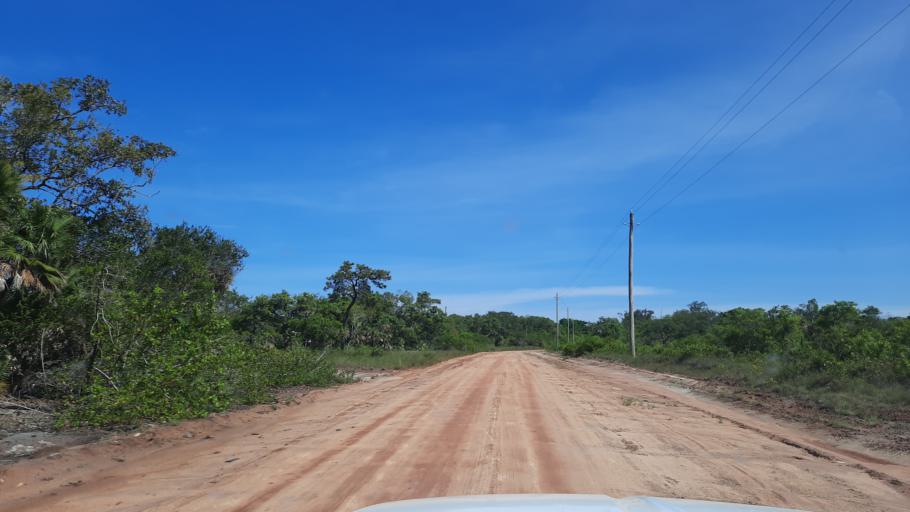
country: BZ
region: Stann Creek
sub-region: Dangriga
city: Dangriga
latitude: 17.1655
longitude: -88.3296
